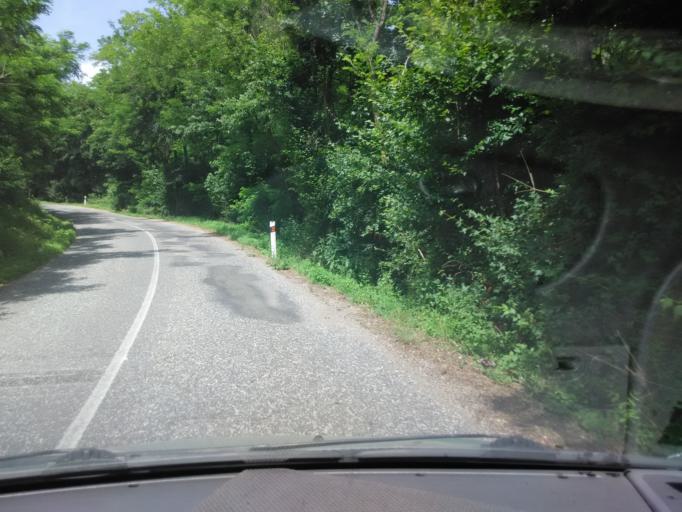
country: SK
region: Nitriansky
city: Levice
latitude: 48.2456
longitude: 18.6870
